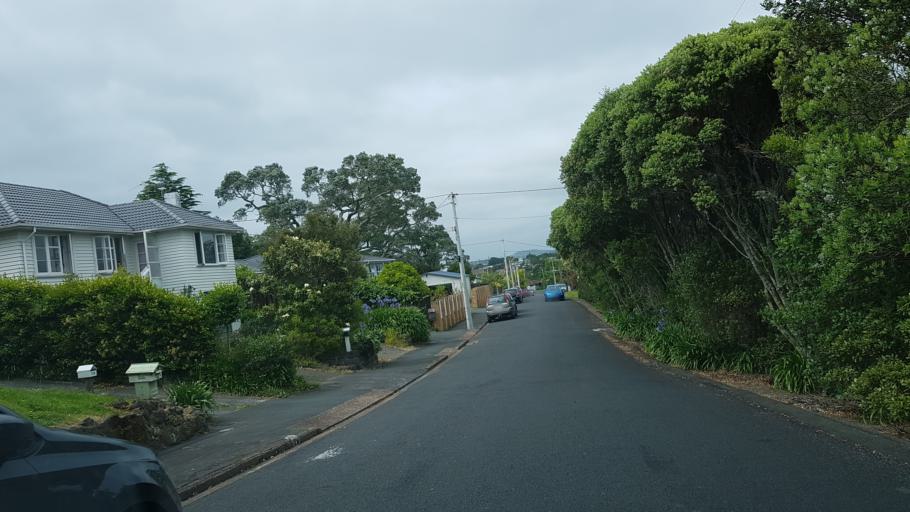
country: NZ
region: Auckland
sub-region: Auckland
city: North Shore
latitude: -36.8049
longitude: 174.7477
